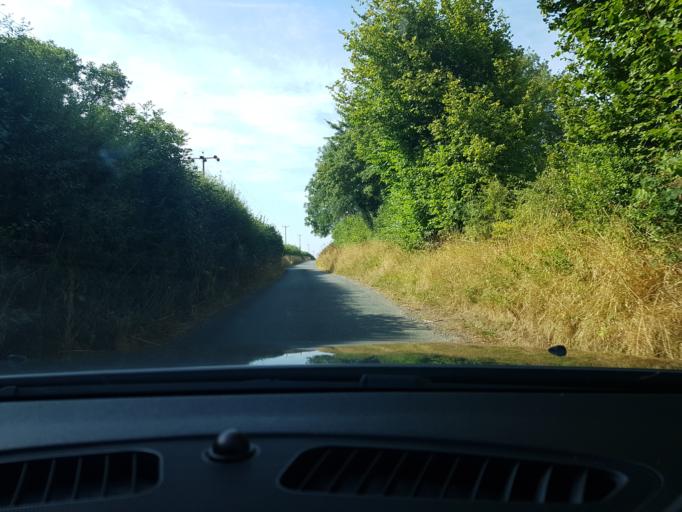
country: GB
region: England
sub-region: West Berkshire
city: Hungerford
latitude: 51.4394
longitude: -1.5069
